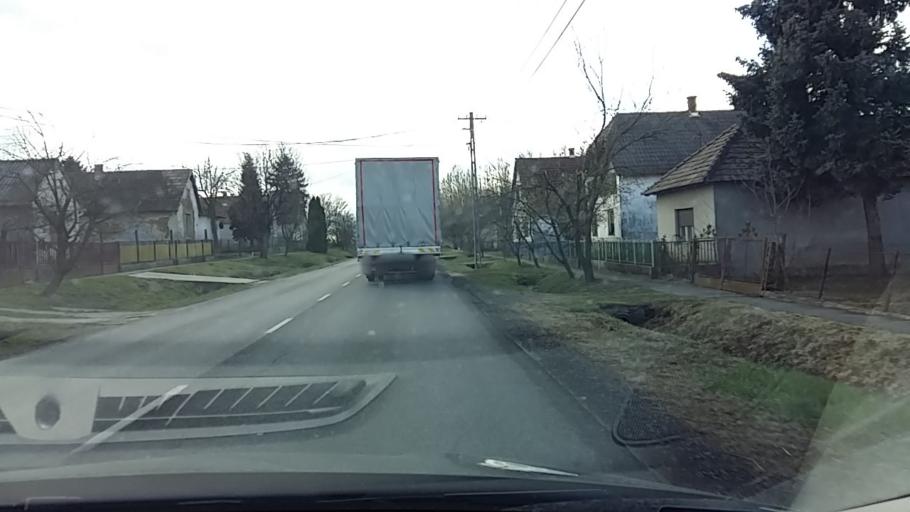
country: HU
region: Somogy
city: Kadarkut
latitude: 46.1954
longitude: 17.6234
